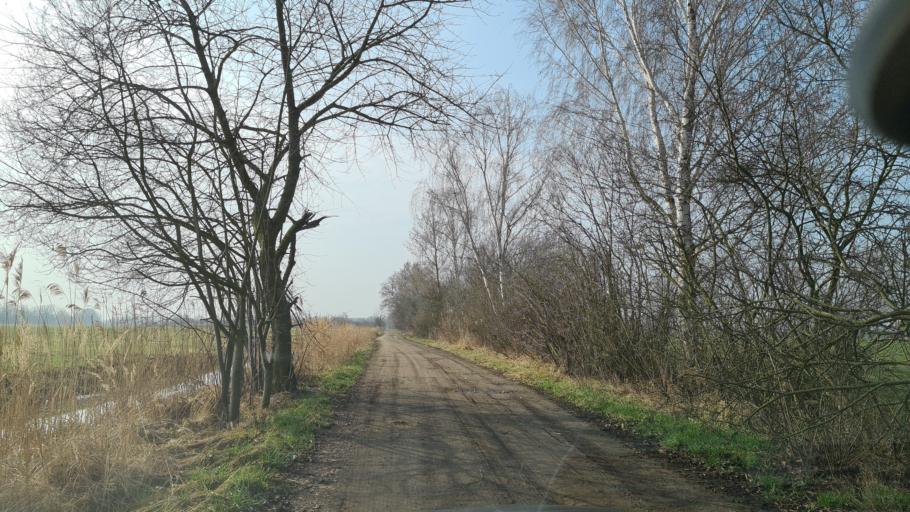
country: DE
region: Brandenburg
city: Bad Liebenwerda
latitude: 51.5397
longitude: 13.3623
